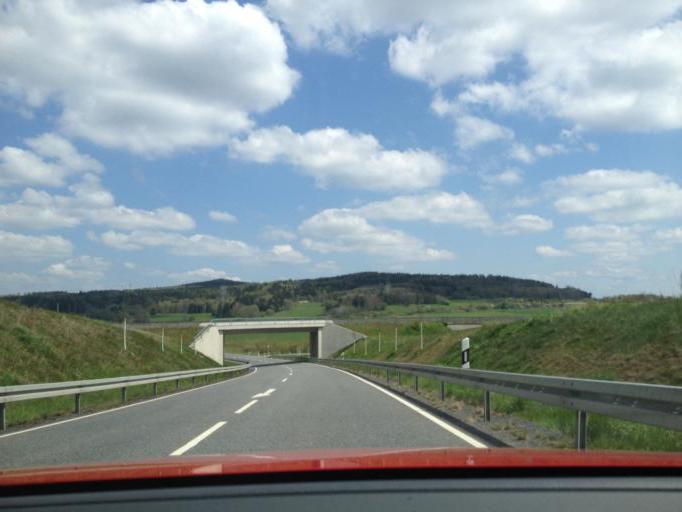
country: DE
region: Bavaria
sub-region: Upper Franconia
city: Marktredwitz
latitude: 49.9815
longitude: 12.1178
